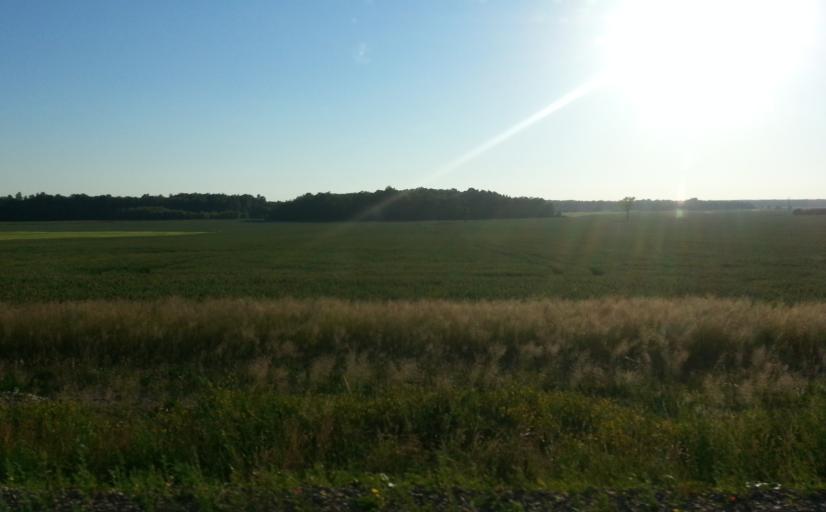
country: LT
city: Ramygala
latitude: 55.6072
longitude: 24.3478
